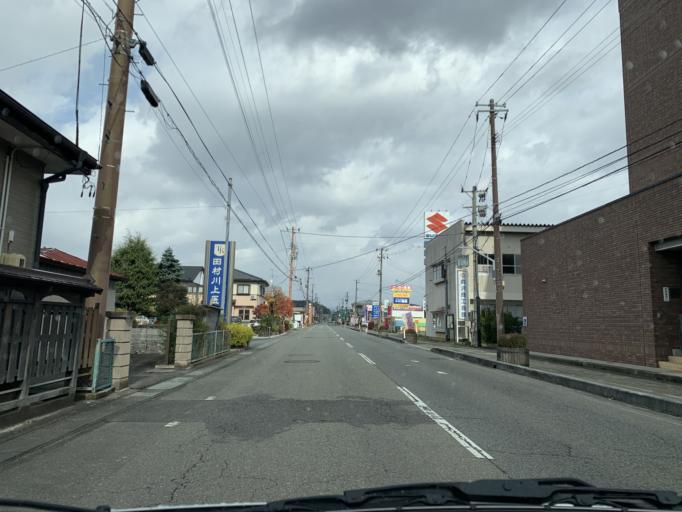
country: JP
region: Iwate
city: Mizusawa
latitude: 39.0511
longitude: 141.1238
